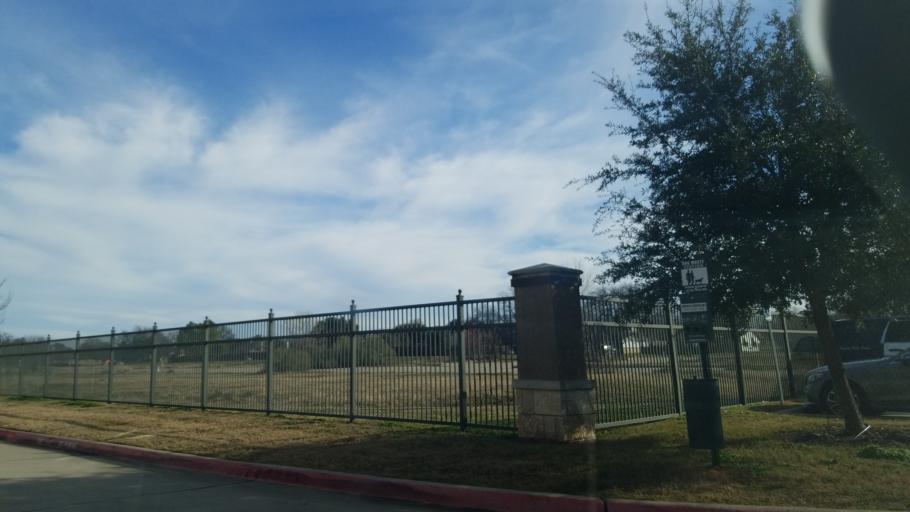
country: US
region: Texas
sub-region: Denton County
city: Corinth
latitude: 33.1457
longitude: -97.0643
